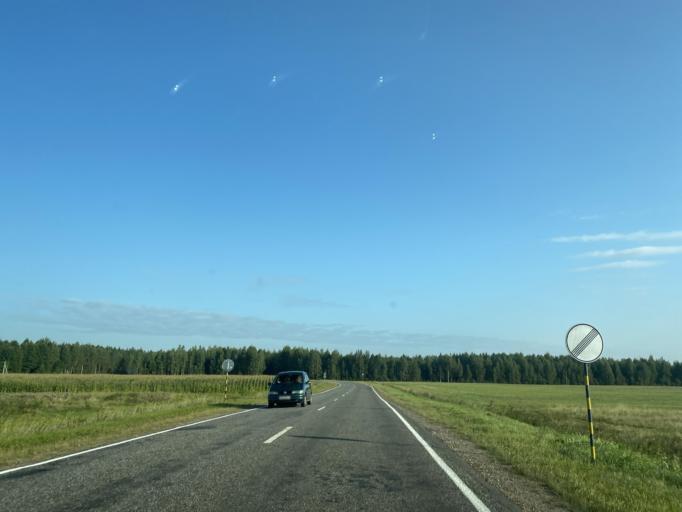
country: BY
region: Minsk
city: Loshnitsa
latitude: 54.0978
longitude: 28.6926
